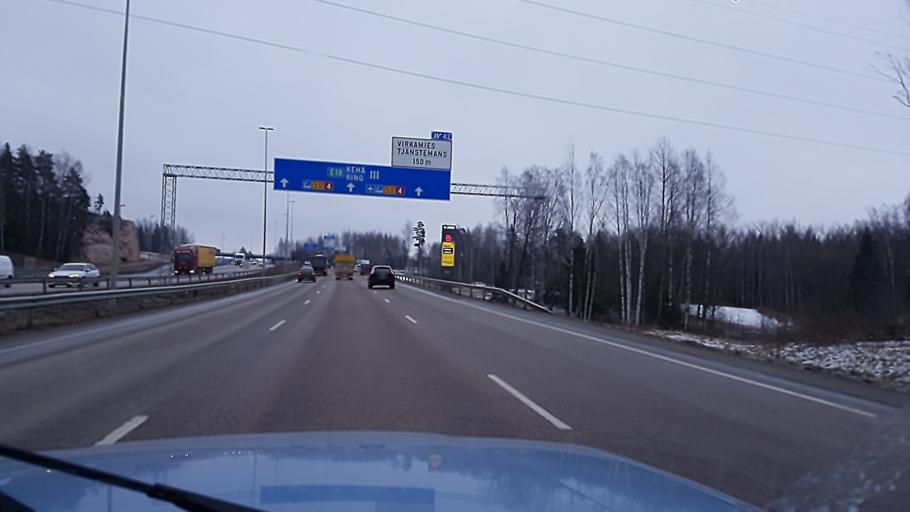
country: FI
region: Uusimaa
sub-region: Helsinki
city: Vantaa
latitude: 60.2965
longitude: 24.9342
